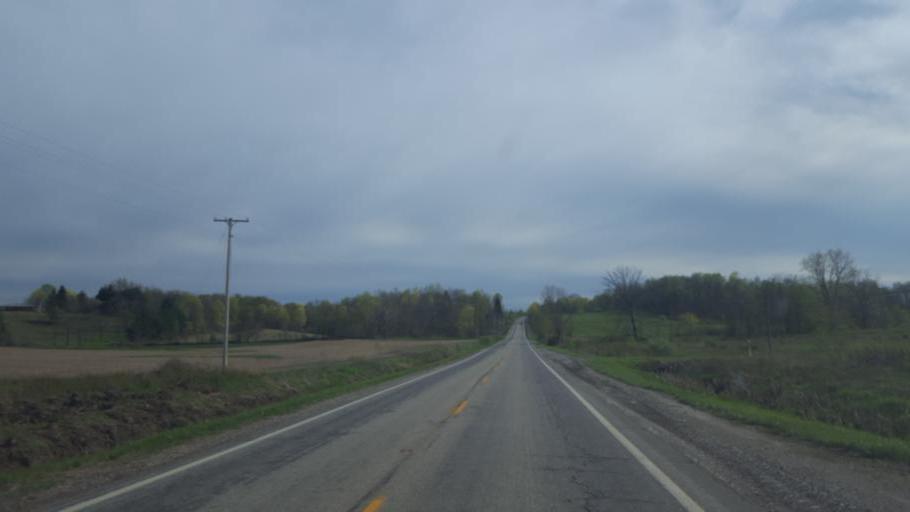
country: US
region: Ohio
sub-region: Knox County
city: Fredericktown
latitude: 40.5148
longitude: -82.6698
